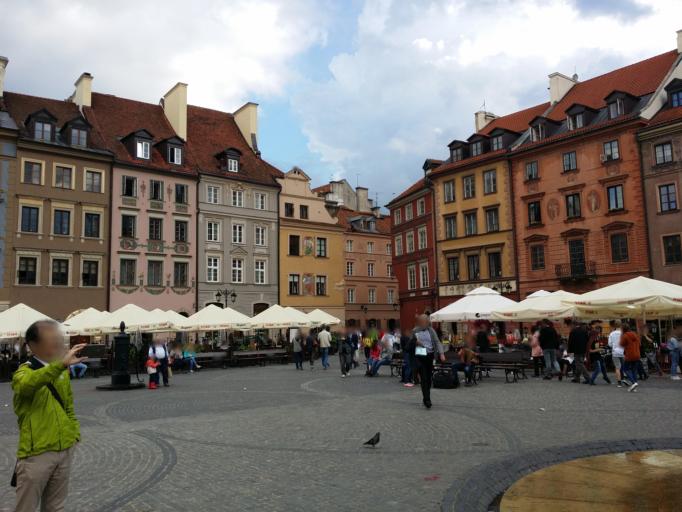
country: PL
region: Masovian Voivodeship
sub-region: Warszawa
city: Warsaw
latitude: 52.2497
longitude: 21.0122
